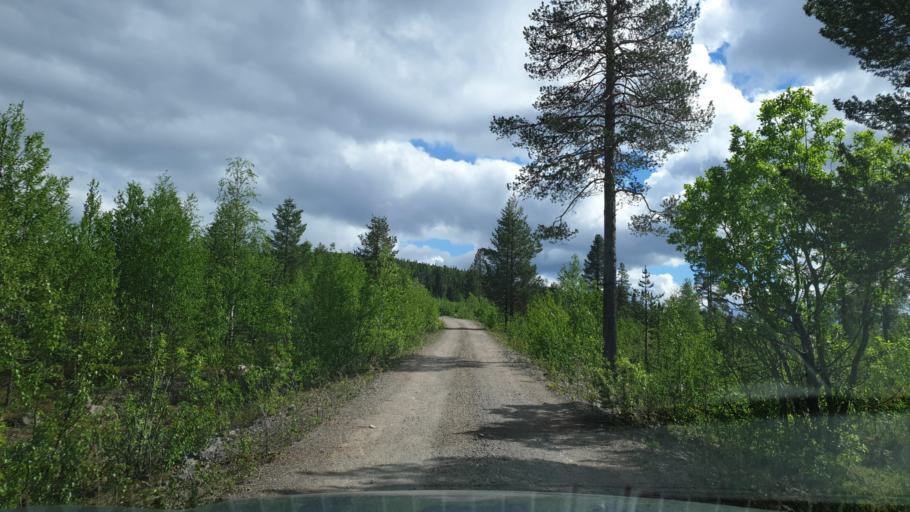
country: SE
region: Norrbotten
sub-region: Jokkmokks Kommun
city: Jokkmokk
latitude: 67.0307
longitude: 20.0008
